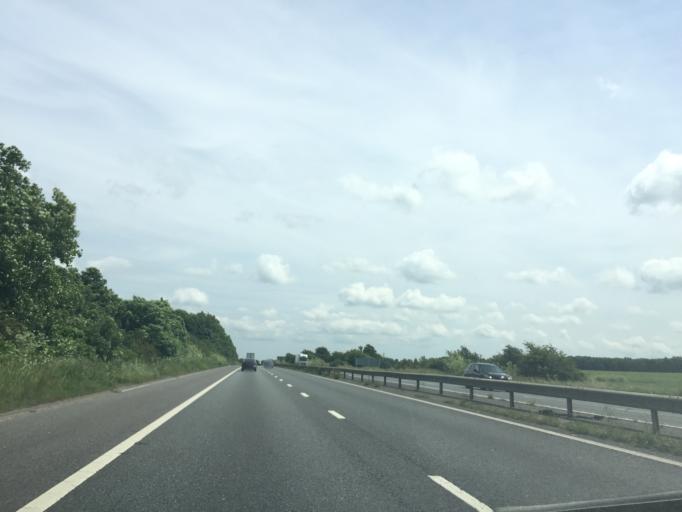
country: GB
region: England
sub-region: Kent
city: Newington
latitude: 51.3255
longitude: 0.6743
